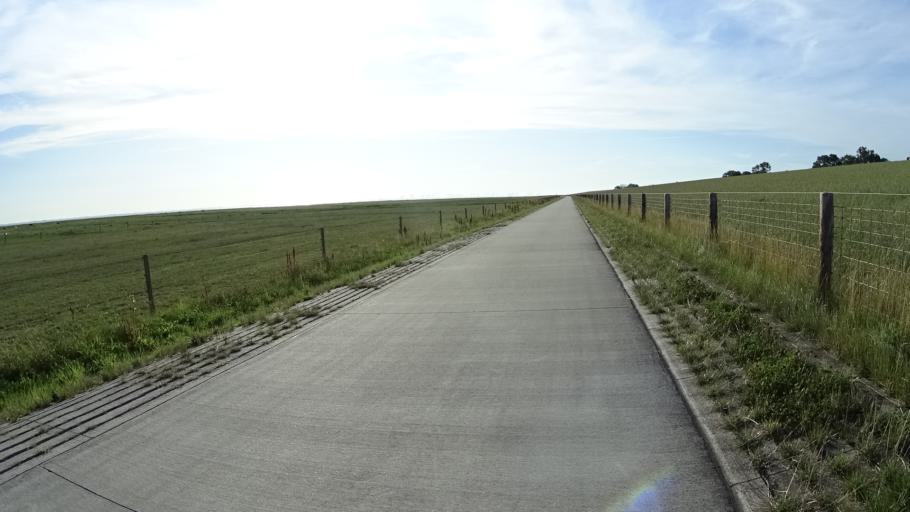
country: DE
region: Lower Saxony
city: Butjadingen
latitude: 53.6058
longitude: 8.3341
